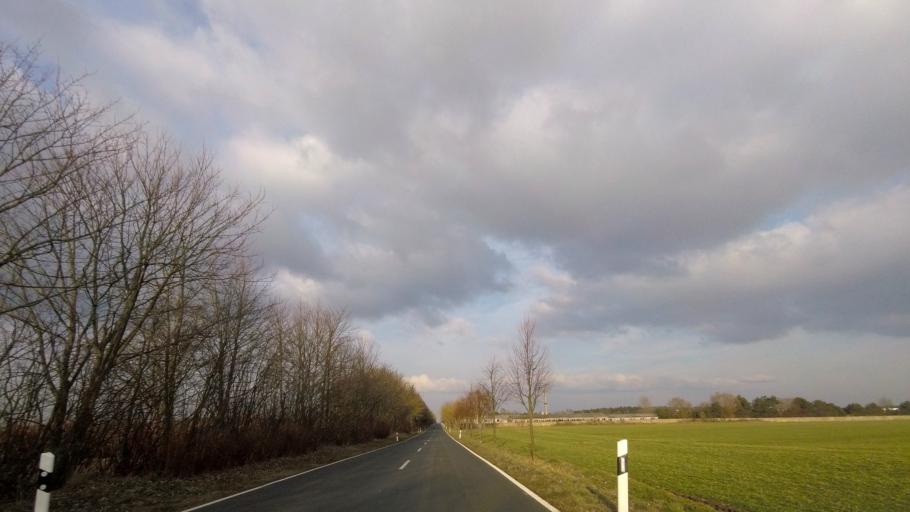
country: DE
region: Brandenburg
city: Belzig
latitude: 52.1139
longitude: 12.5744
